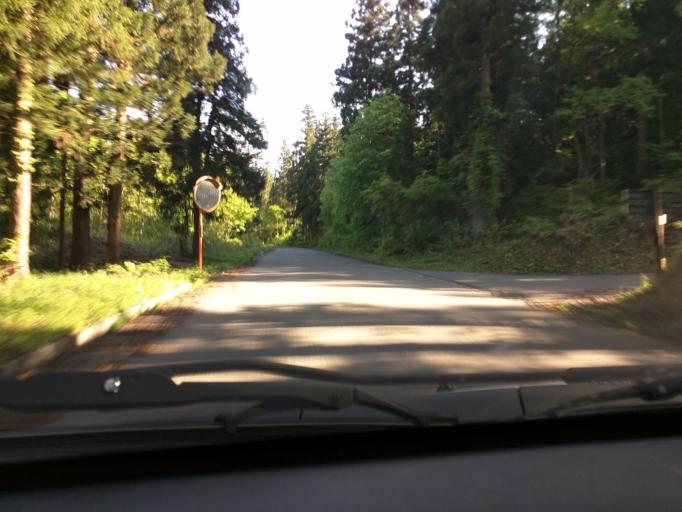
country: JP
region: Fukushima
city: Kitakata
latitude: 37.4834
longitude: 139.6691
